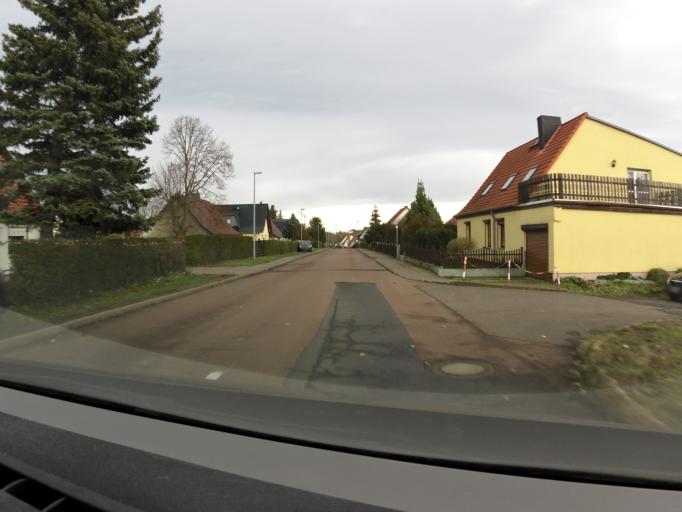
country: DE
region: Saxony-Anhalt
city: Gerbstedt
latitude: 51.6426
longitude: 11.6216
